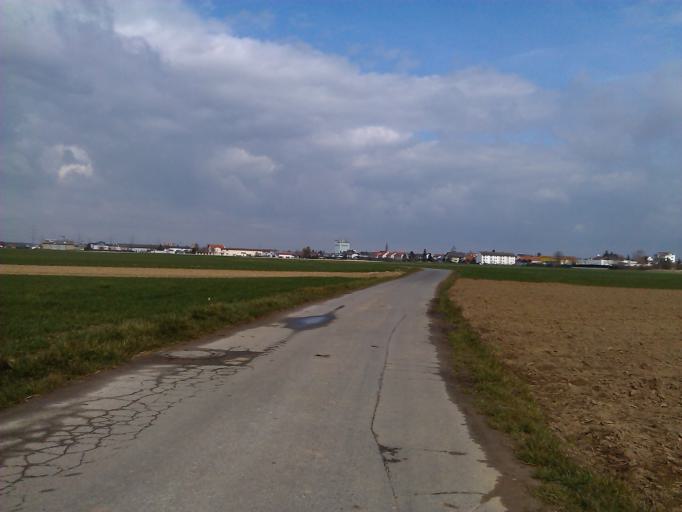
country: DE
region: Hesse
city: Pfungstadt
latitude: 49.7893
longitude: 8.5970
